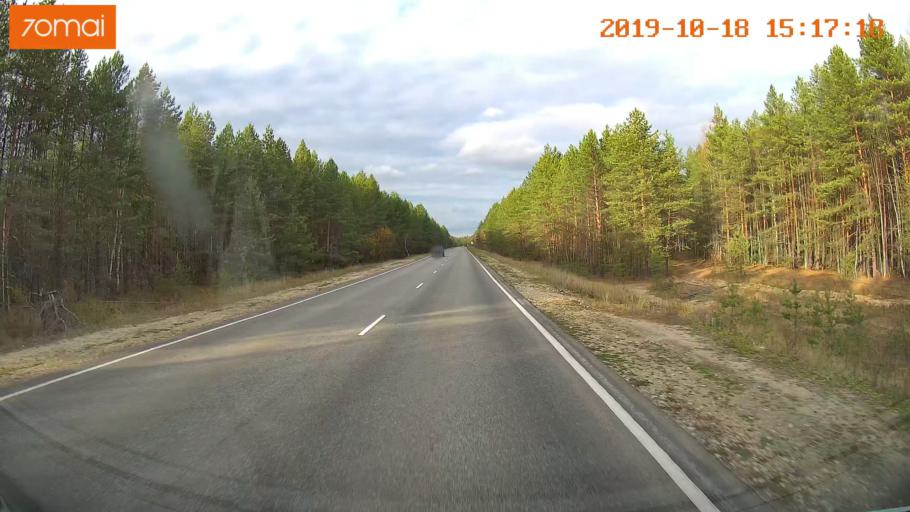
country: RU
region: Vladimir
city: Anopino
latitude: 55.6477
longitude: 40.7263
